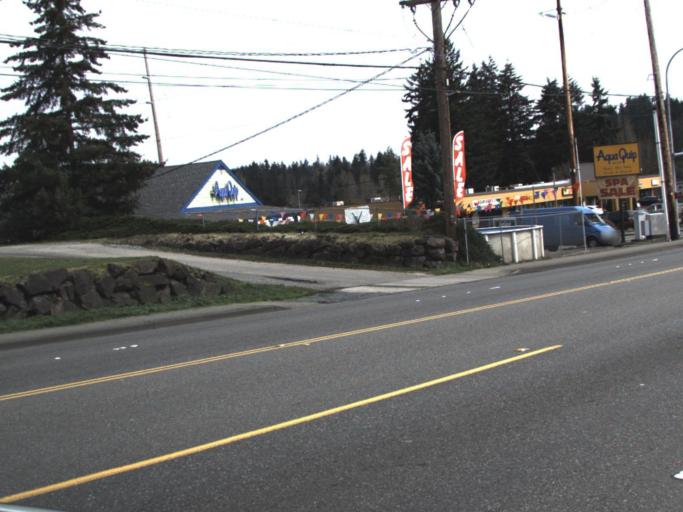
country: US
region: Washington
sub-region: King County
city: Covington
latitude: 47.3580
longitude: -122.1399
